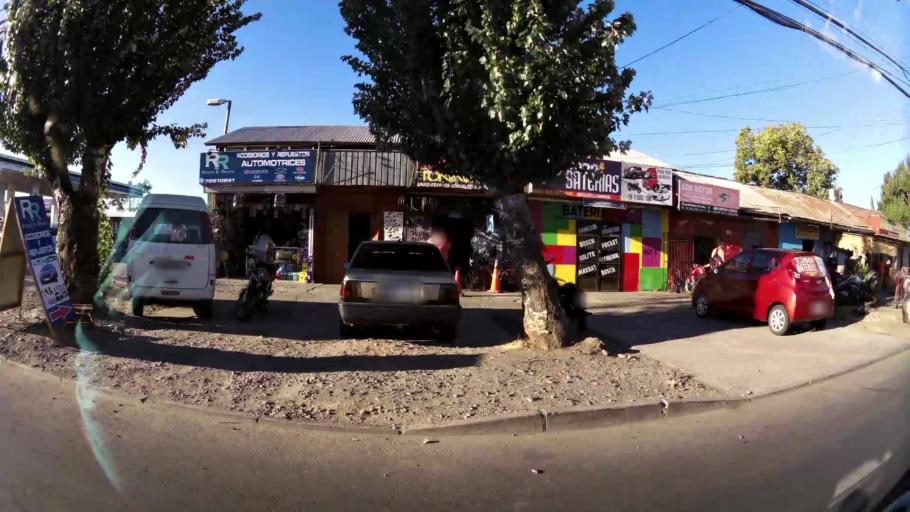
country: CL
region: Maule
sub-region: Provincia de Curico
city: Curico
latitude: -34.9766
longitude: -71.2446
